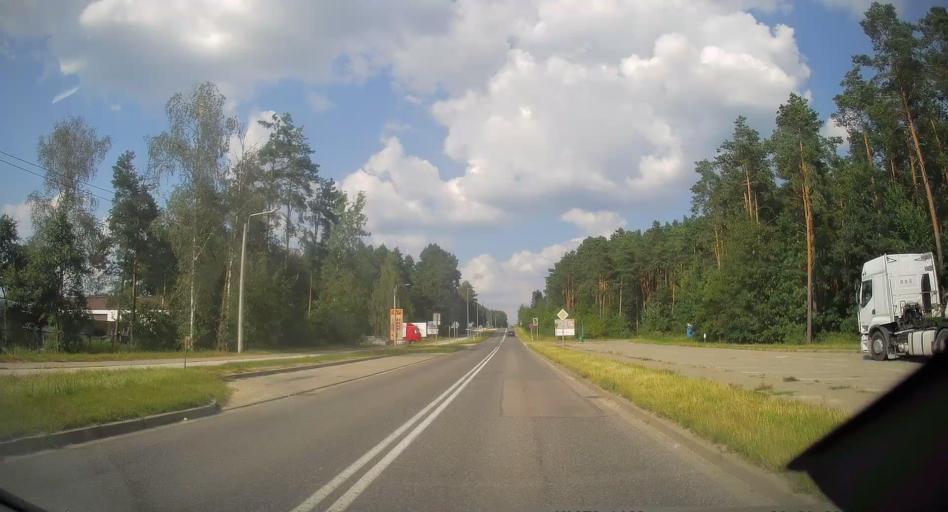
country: PL
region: Swietokrzyskie
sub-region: Powiat kielecki
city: Lopuszno
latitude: 50.9384
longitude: 20.2432
